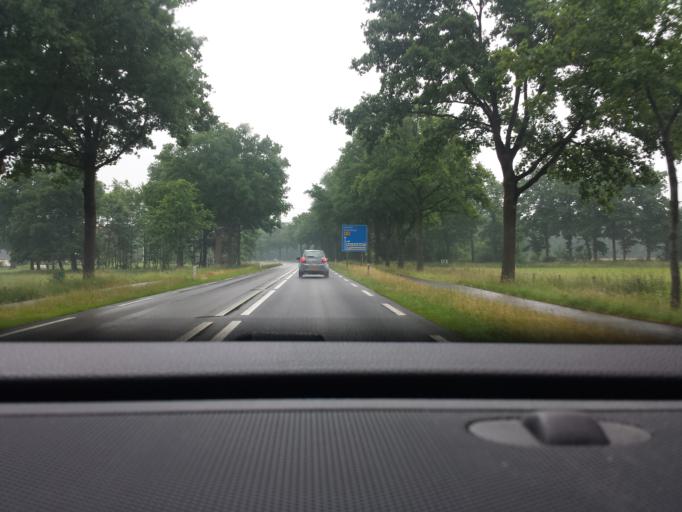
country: NL
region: Overijssel
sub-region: Gemeente Enschede
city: Enschede
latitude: 52.1919
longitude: 6.8236
